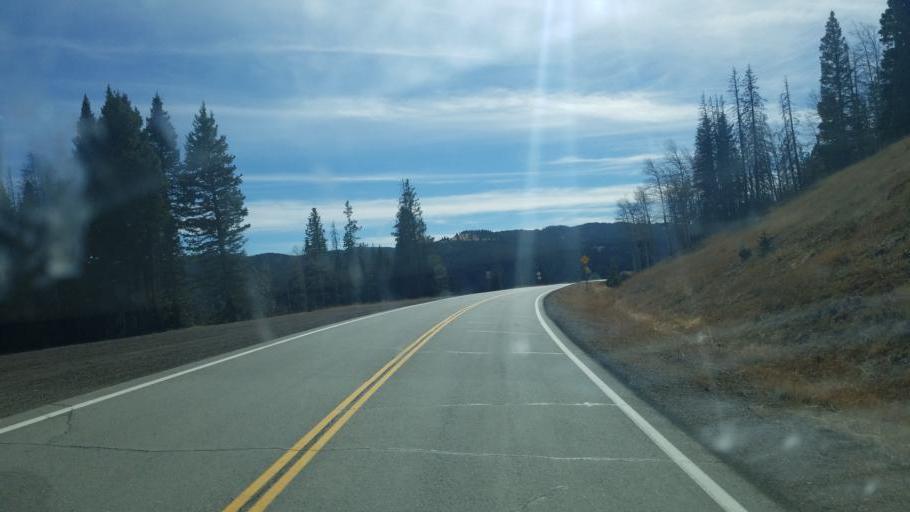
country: US
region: New Mexico
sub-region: Rio Arriba County
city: Chama
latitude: 37.0180
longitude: -106.4168
